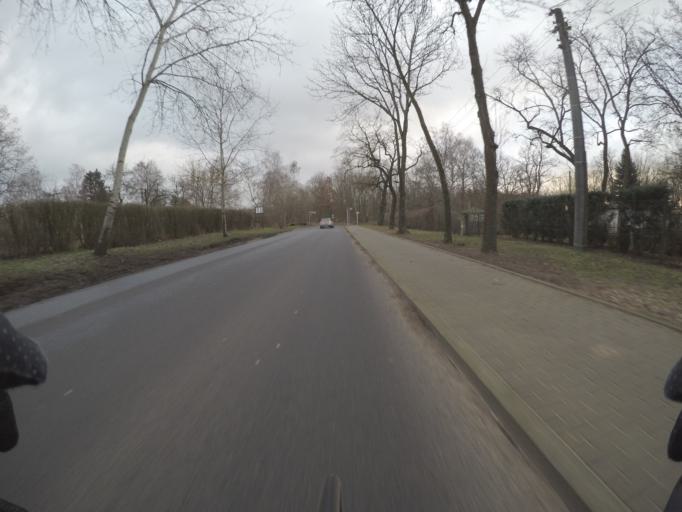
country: DE
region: Berlin
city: Karlshorst
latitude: 52.4739
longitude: 13.5472
